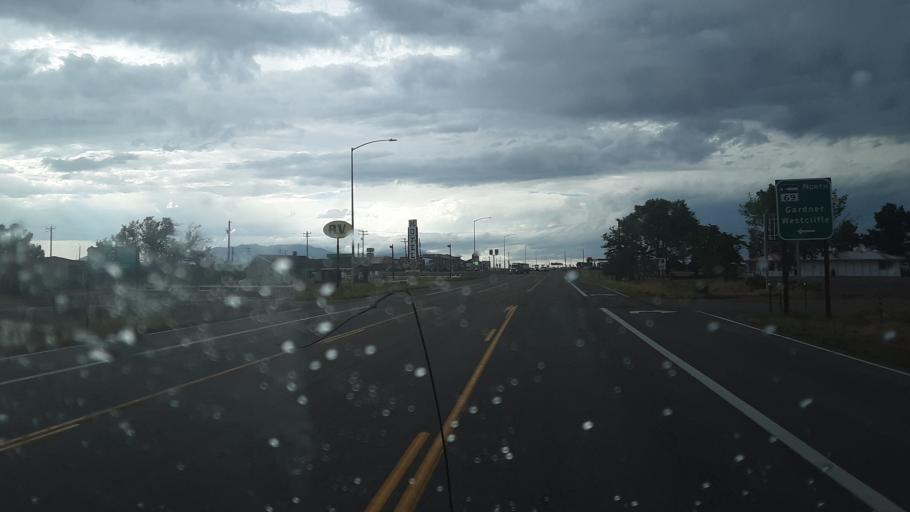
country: US
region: Colorado
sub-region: Huerfano County
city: Walsenburg
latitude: 37.6513
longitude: -104.7919
